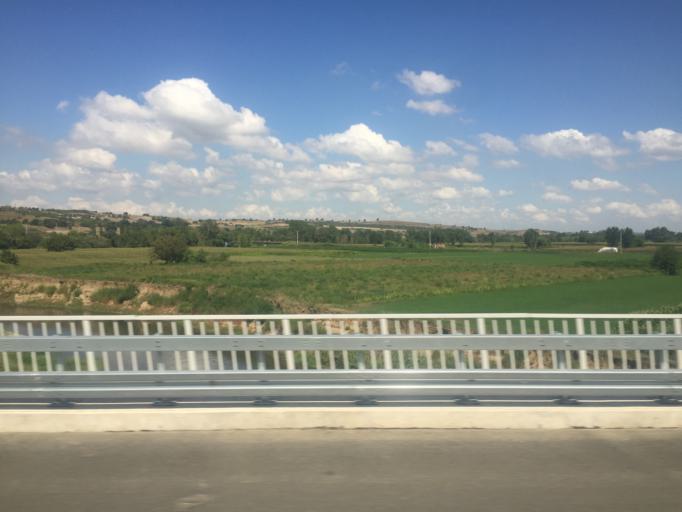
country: TR
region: Balikesir
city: Gobel
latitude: 39.9827
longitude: 28.1797
